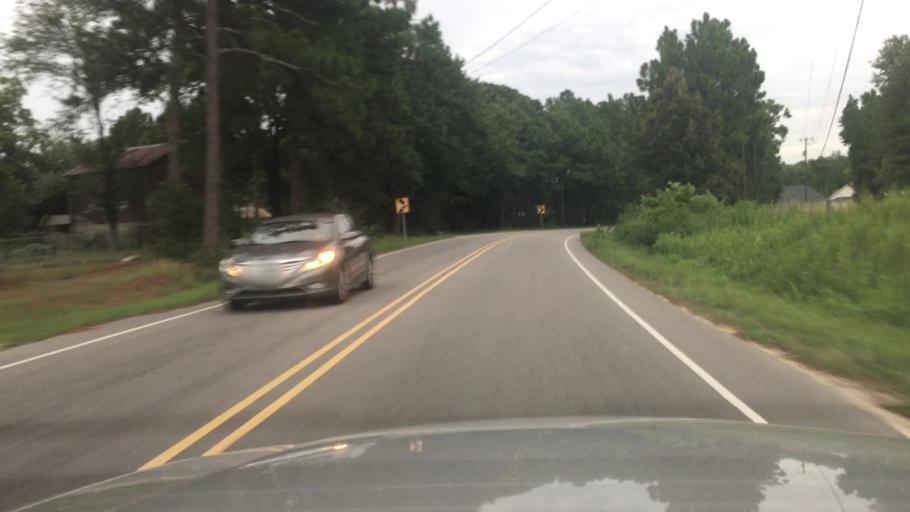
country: US
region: North Carolina
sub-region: Hoke County
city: Rockfish
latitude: 34.9886
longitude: -79.0279
